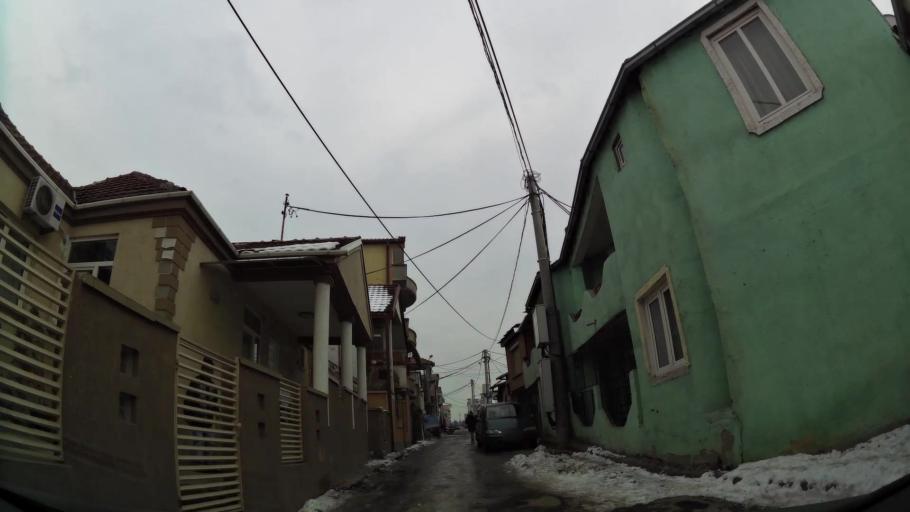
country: MK
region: Suto Orizari
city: Suto Orizare
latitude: 42.0453
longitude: 21.4251
